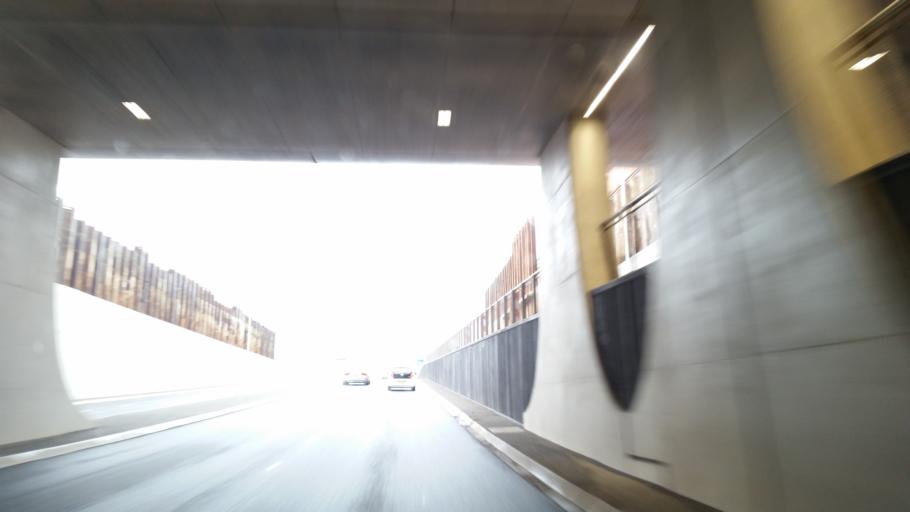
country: NL
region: Friesland
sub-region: Gemeente Leeuwarden
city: Huizum
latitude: 53.1850
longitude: 5.8190
